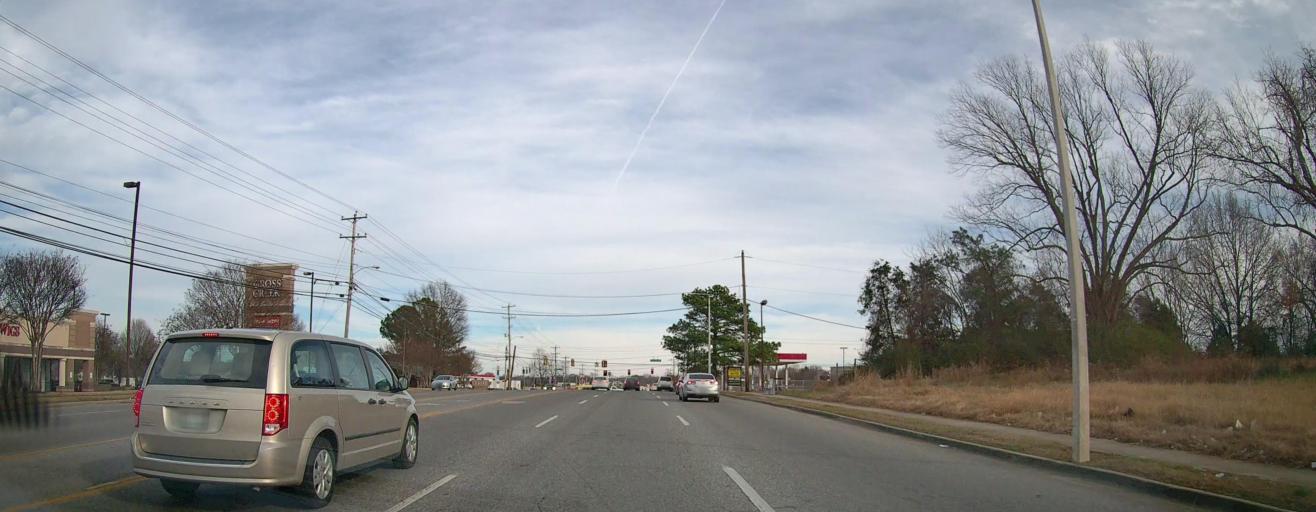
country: US
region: Tennessee
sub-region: Shelby County
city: Germantown
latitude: 35.0492
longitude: -89.8320
